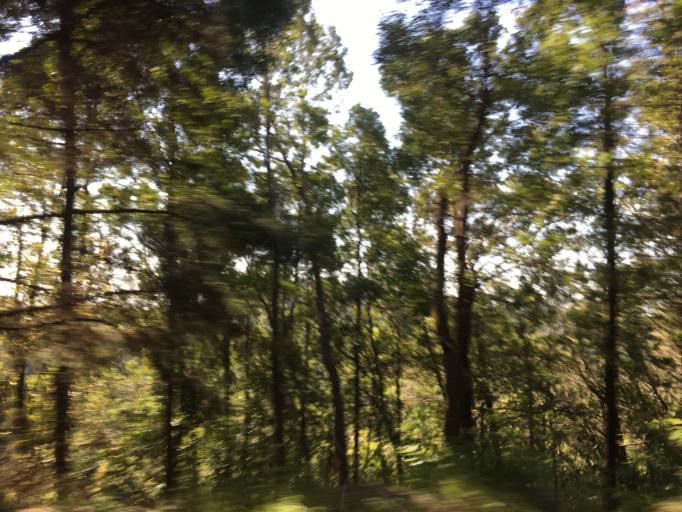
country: PT
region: Lisbon
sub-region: Sintra
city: Colares
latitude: 38.7697
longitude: -9.4424
